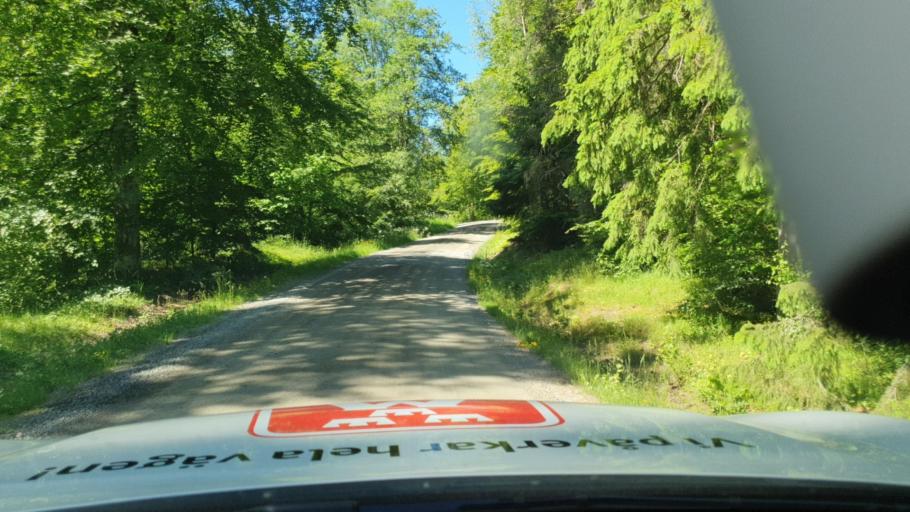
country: SE
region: Joenkoeping
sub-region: Mullsjo Kommun
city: Mullsjoe
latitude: 57.8915
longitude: 13.9500
